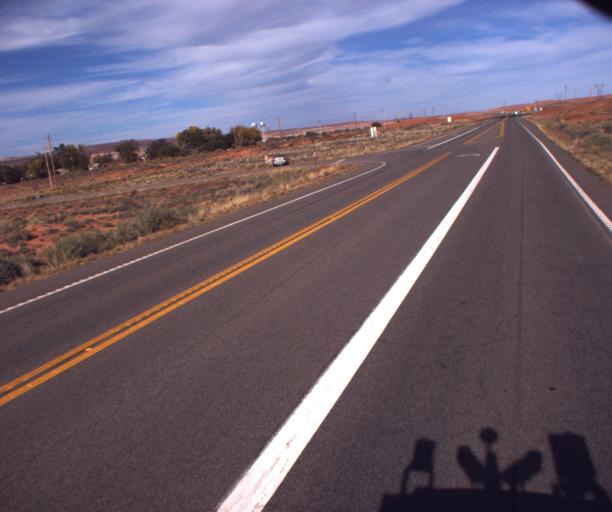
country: US
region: Arizona
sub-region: Navajo County
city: Kayenta
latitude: 36.8356
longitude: -109.8510
